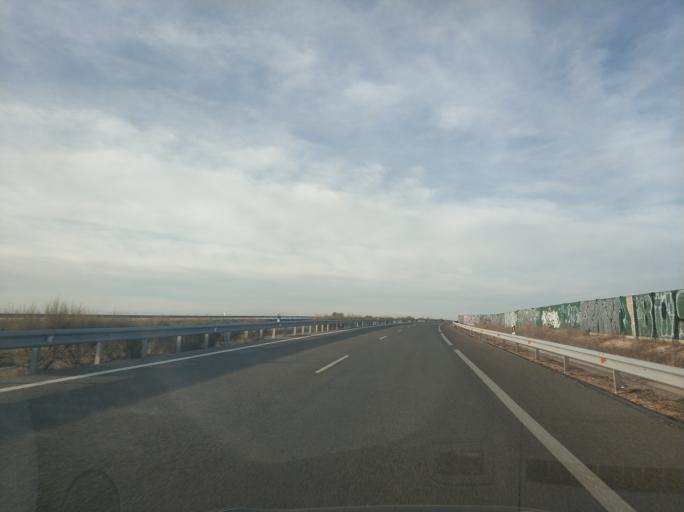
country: ES
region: Castille and Leon
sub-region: Provincia de Salamanca
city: Villamayor
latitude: 41.0167
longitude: -5.6797
